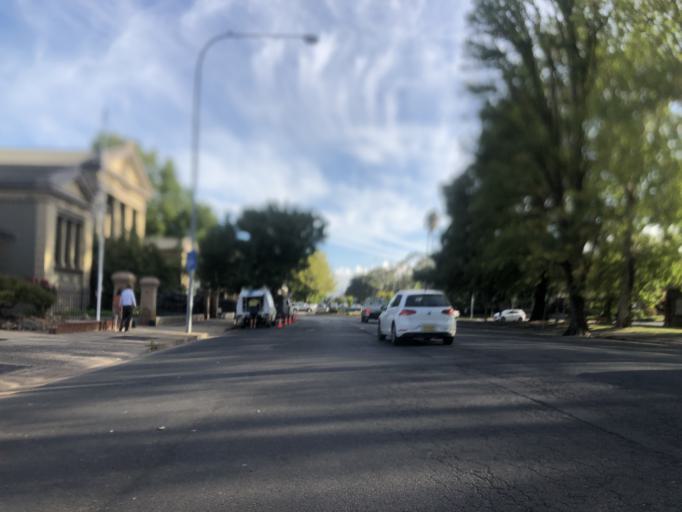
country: AU
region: New South Wales
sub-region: Orange Municipality
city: Orange
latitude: -33.2825
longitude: 149.1014
